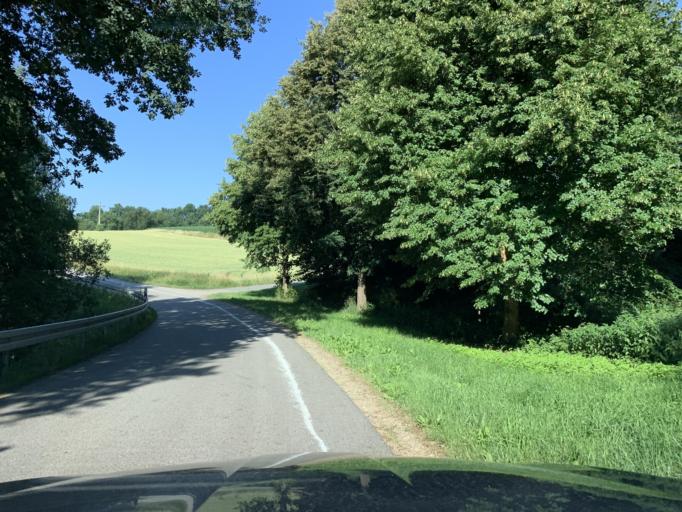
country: DE
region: Bavaria
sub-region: Upper Palatinate
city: Dieterskirchen
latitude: 49.4170
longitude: 12.4212
